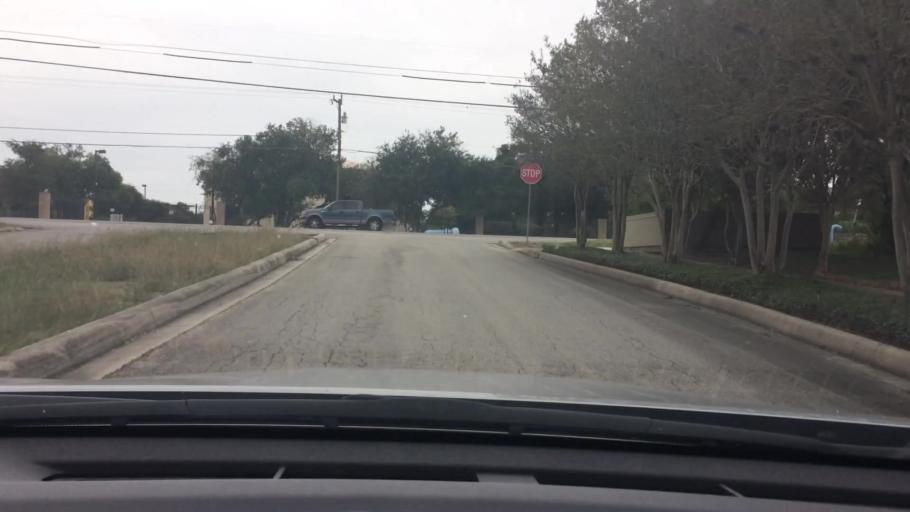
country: US
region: Texas
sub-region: Bexar County
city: Windcrest
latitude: 29.5395
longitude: -98.3717
